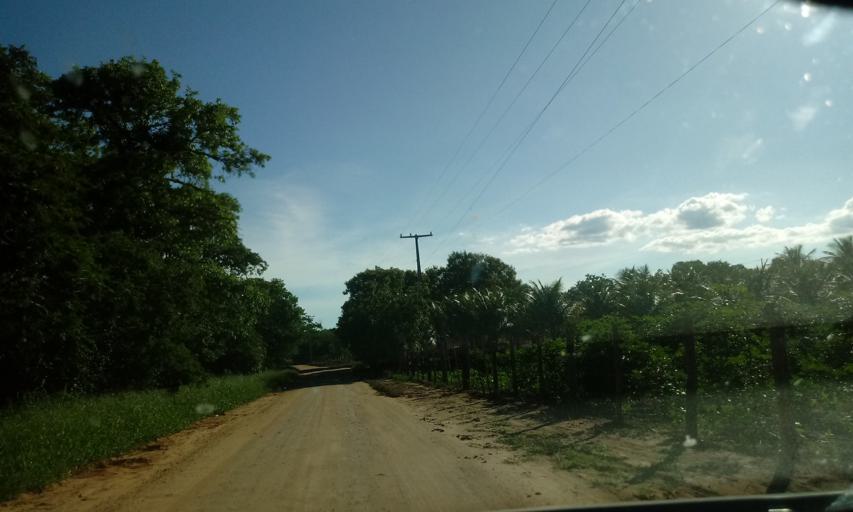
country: BR
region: Bahia
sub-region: Riacho De Santana
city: Riacho de Santana
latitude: -13.7903
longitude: -42.7297
